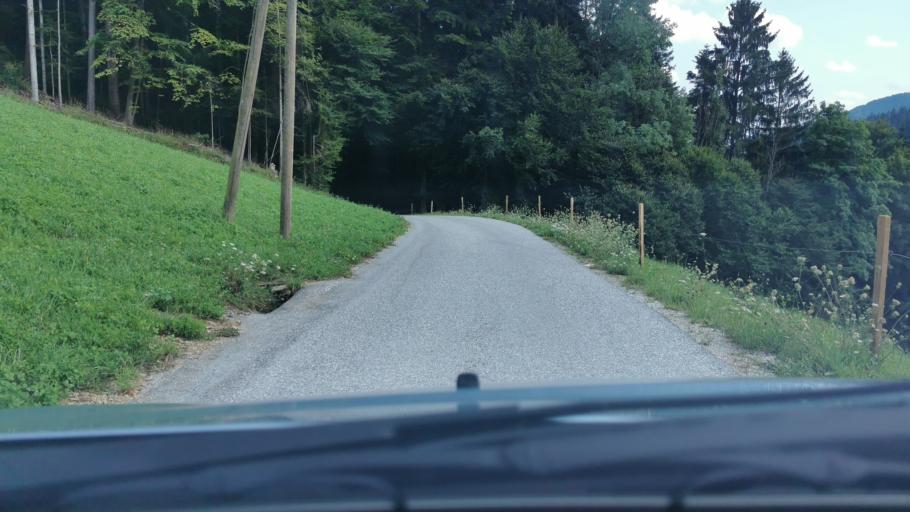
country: AT
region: Styria
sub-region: Politischer Bezirk Weiz
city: Koglhof
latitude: 47.3234
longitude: 15.6656
